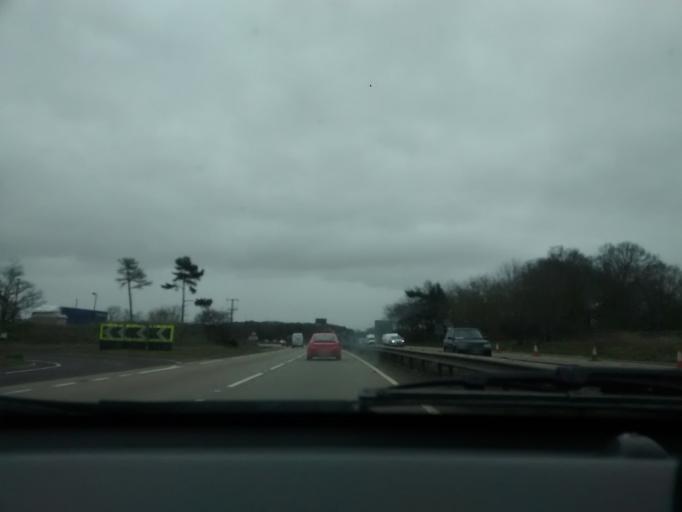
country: GB
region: England
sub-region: Suffolk
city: Kesgrave
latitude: 52.0248
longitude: 1.2260
